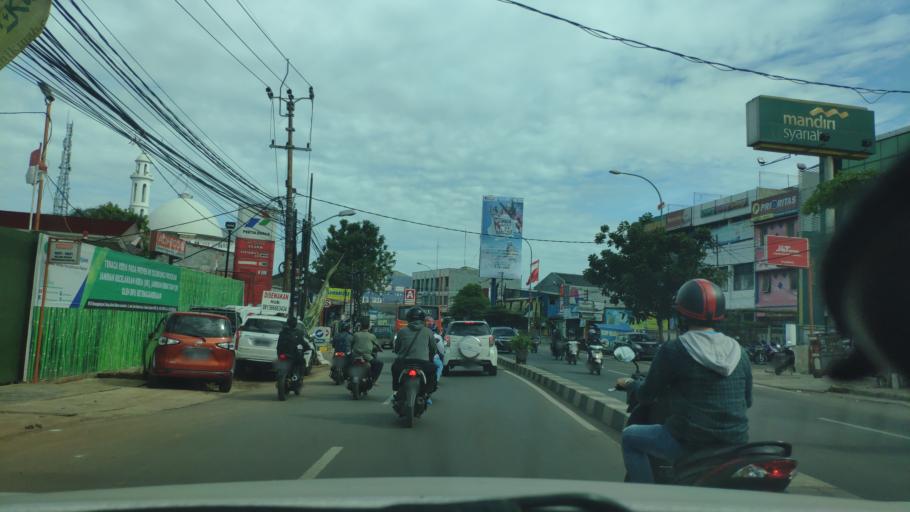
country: ID
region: West Java
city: Ciputat
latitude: -6.2256
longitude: 106.7119
